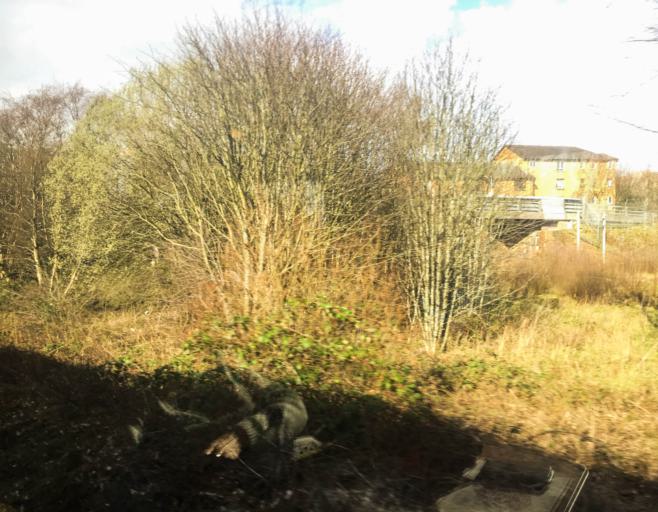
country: GB
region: Scotland
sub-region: East Dunbartonshire
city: Bishopbriggs
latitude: 55.8770
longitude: -4.2234
